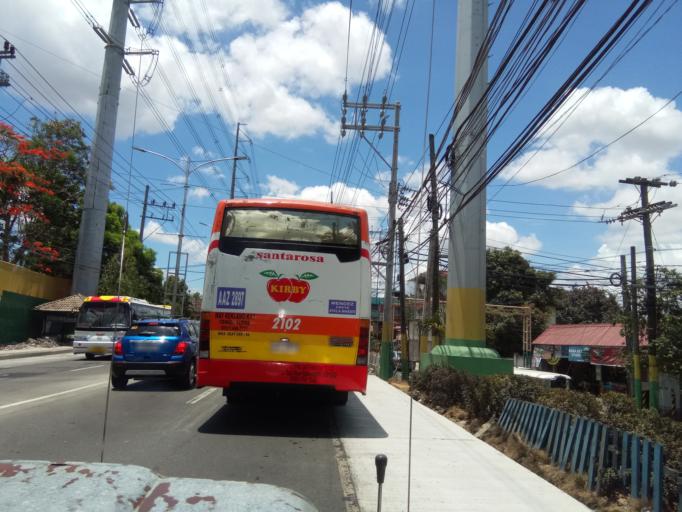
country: PH
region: Calabarzon
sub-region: Province of Cavite
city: Dasmarinas
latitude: 14.3172
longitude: 120.9434
